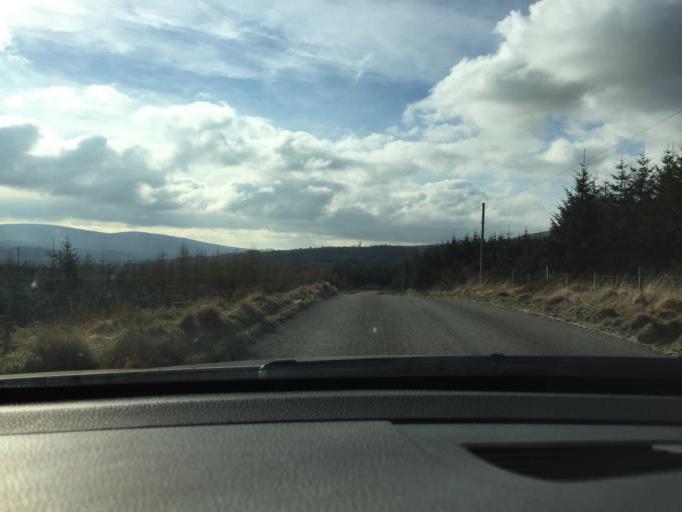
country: IE
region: Leinster
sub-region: Wicklow
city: Valleymount
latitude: 53.0596
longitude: -6.4493
